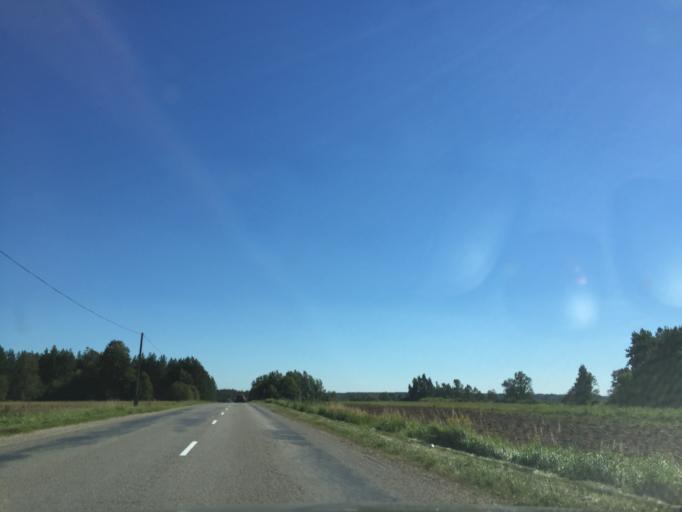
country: LV
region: Akniste
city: Akniste
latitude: 56.1326
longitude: 25.8255
